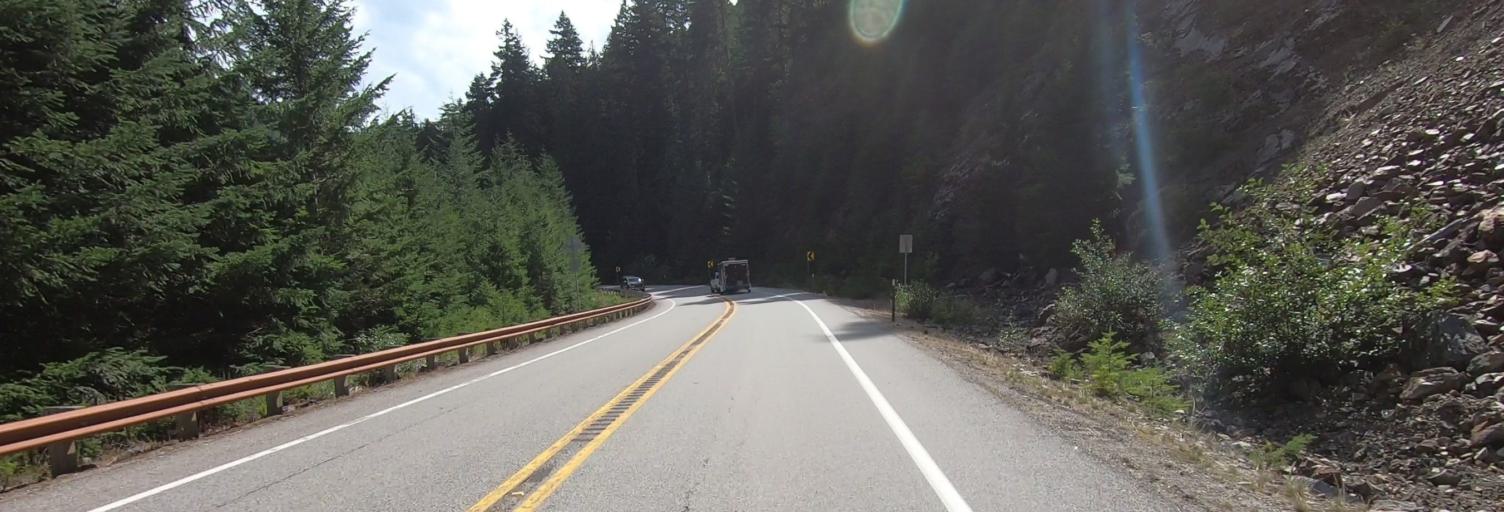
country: US
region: Washington
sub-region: Snohomish County
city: Darrington
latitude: 48.6854
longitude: -120.8969
